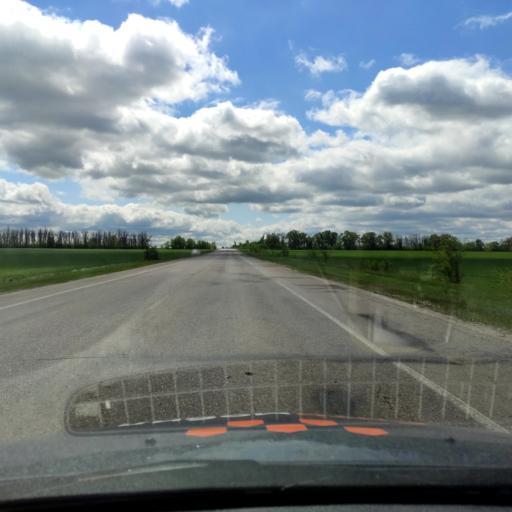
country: RU
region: Voronezj
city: Novaya Usman'
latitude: 51.5935
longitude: 39.3383
